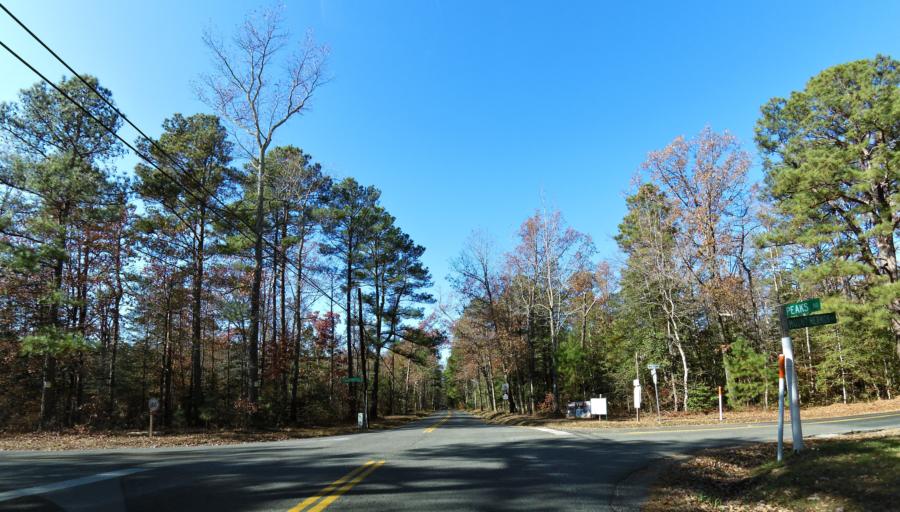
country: US
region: Virginia
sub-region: Hanover County
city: Hanover
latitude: 37.7154
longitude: -77.4130
